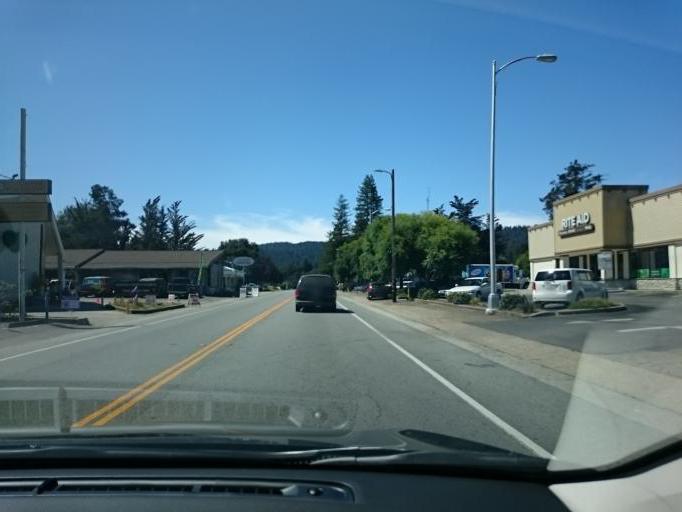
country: US
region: California
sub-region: Santa Cruz County
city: Felton
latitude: 37.0505
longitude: -122.0733
